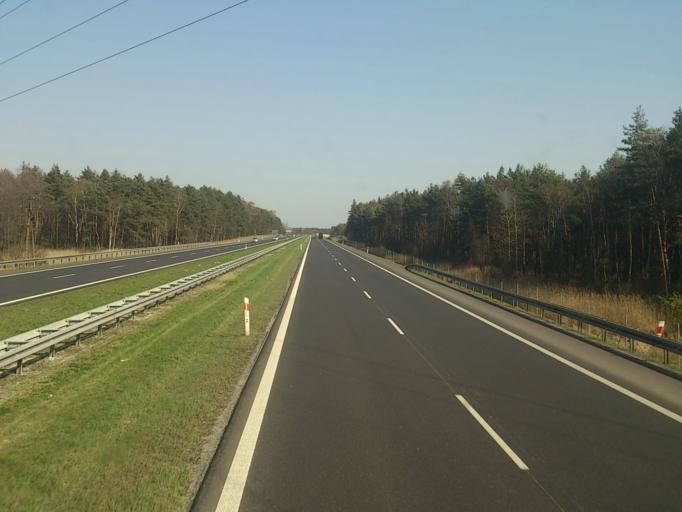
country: PL
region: Lesser Poland Voivodeship
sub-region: Powiat chrzanowski
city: Trzebinia
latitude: 50.1425
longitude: 19.4482
